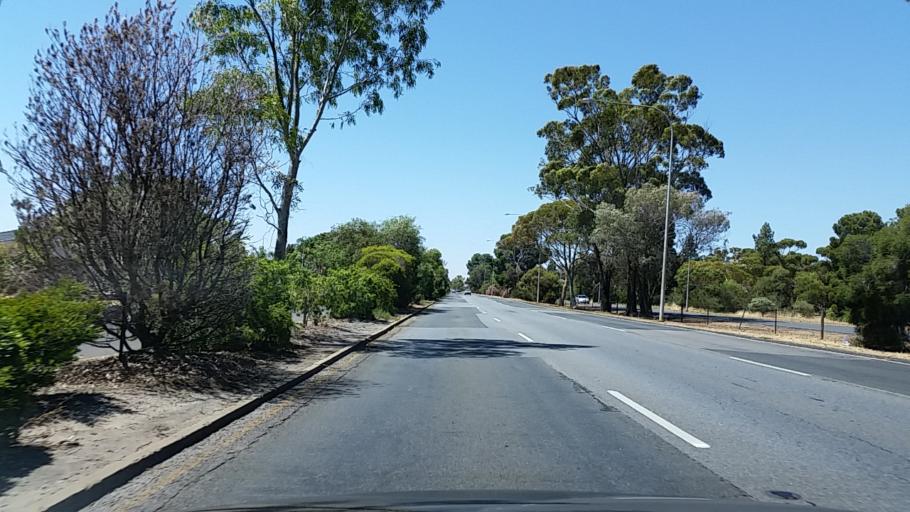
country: AU
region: South Australia
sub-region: Salisbury
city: Elizabeth
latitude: -34.7122
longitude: 138.6753
